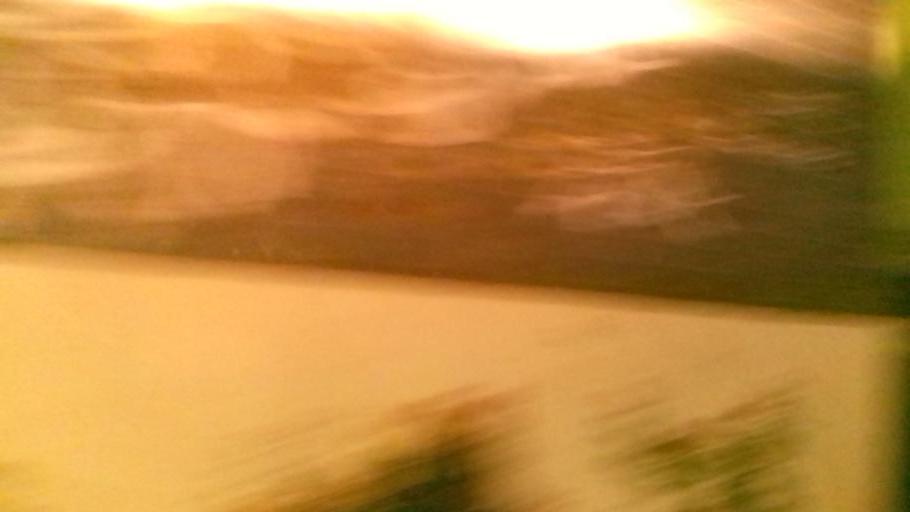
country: BR
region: Minas Gerais
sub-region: Belo Horizonte
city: Belo Horizonte
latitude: -19.9014
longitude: -43.9588
